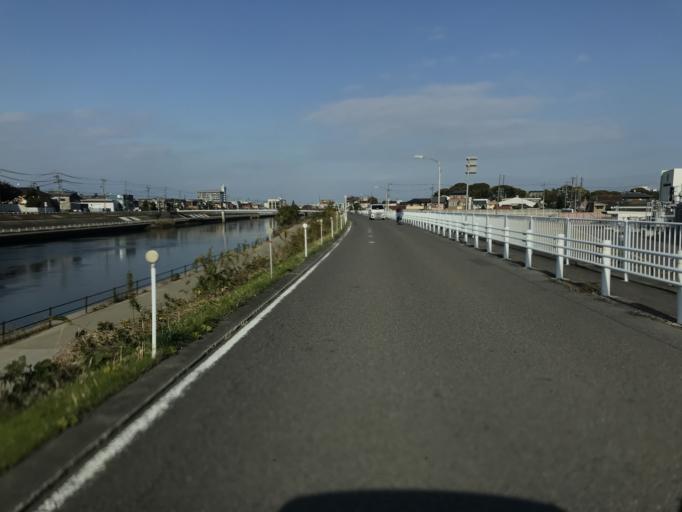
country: JP
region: Aichi
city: Nagoya-shi
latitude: 35.1891
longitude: 136.8484
